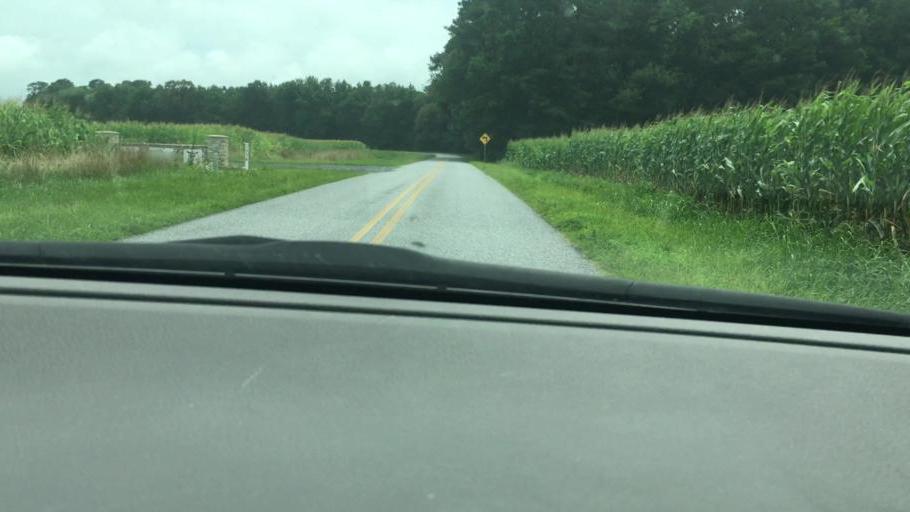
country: US
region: Maryland
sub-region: Worcester County
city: Pocomoke City
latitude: 38.0620
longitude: -75.5053
